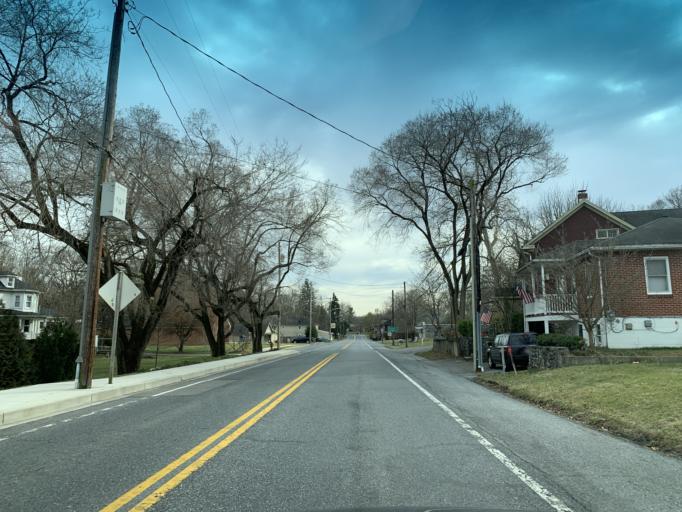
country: US
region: Maryland
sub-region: Washington County
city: Hagerstown
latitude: 39.6079
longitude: -77.7053
